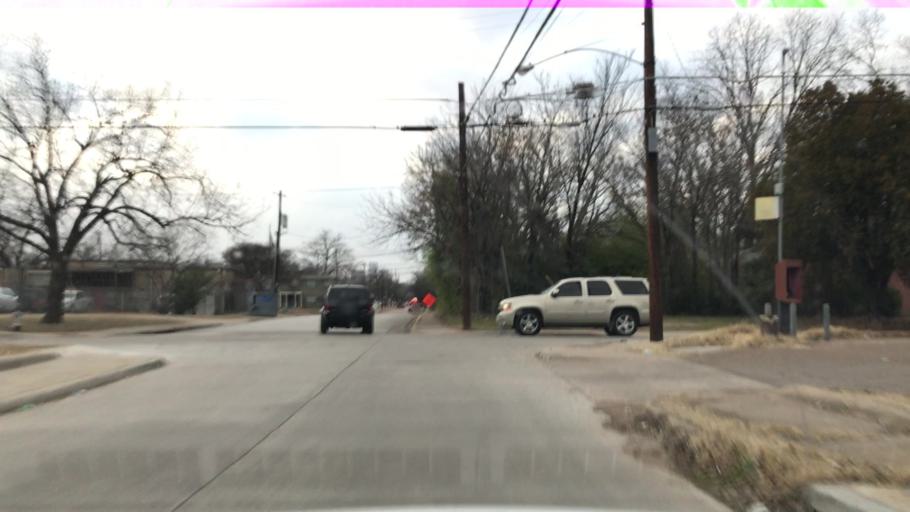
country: US
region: Texas
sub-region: Dallas County
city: Dallas
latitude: 32.7517
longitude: -96.7563
